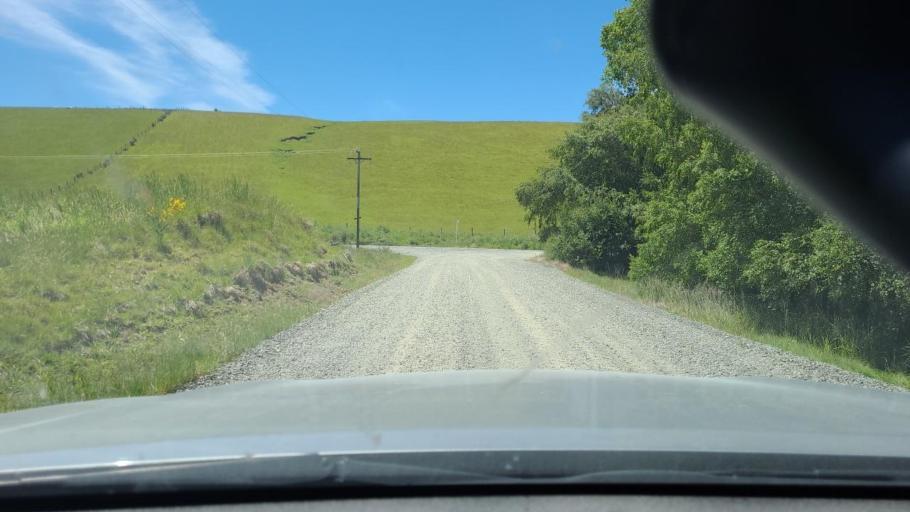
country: NZ
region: Southland
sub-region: Southland District
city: Te Anau
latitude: -45.4906
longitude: 167.8359
